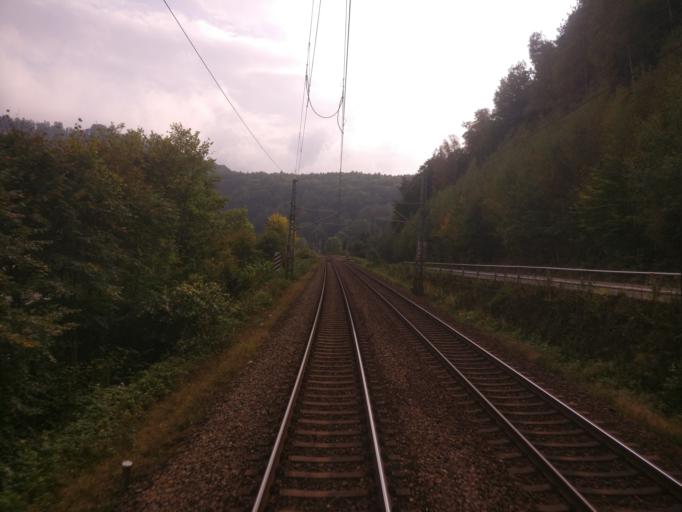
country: DE
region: Saxony
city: Konigstein
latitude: 50.9323
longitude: 14.0573
